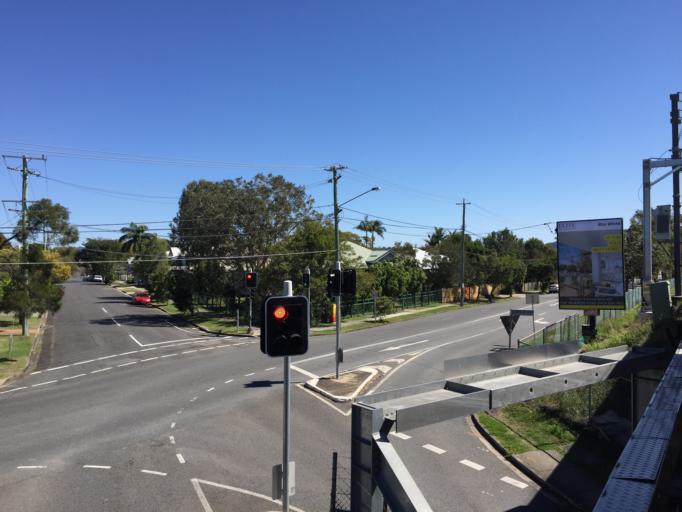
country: AU
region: Queensland
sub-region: Brisbane
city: Rocklea
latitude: -27.5246
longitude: 152.9777
